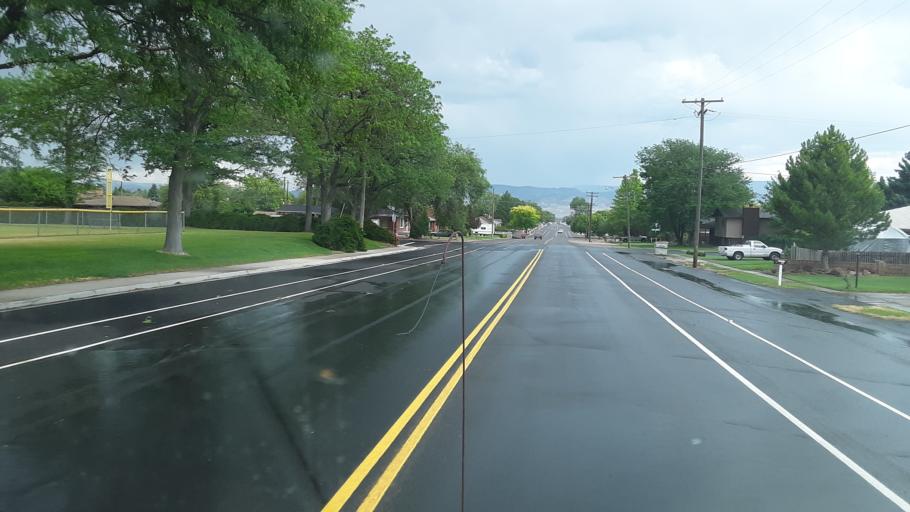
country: US
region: Utah
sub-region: Sevier County
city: Richfield
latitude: 38.7723
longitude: -112.0964
